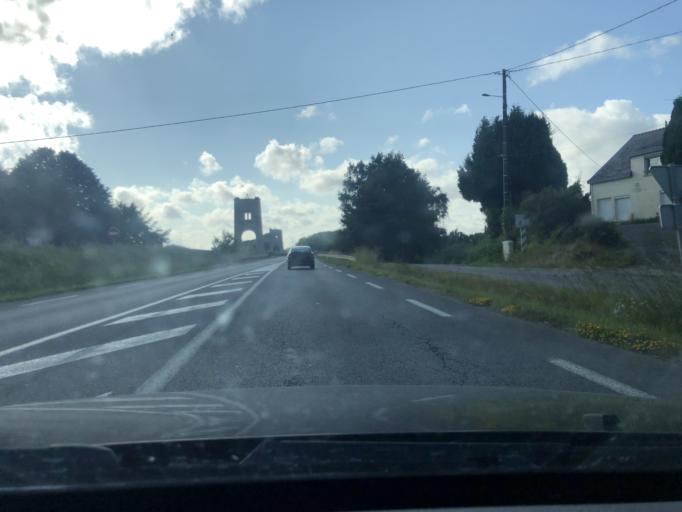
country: FR
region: Brittany
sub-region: Departement du Morbihan
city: Lanester
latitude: 47.7639
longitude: -3.2989
